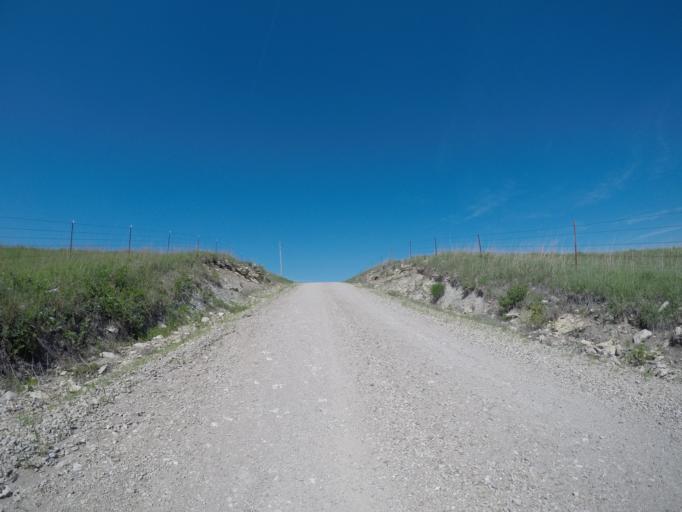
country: US
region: Kansas
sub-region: Wabaunsee County
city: Alma
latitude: 39.0151
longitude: -96.1666
